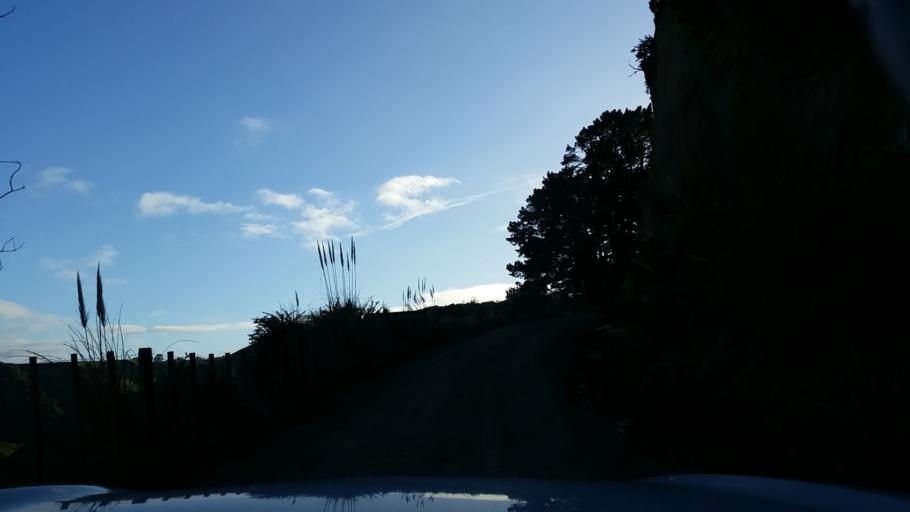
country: NZ
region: Taranaki
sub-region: South Taranaki District
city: Patea
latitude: -39.7580
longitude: 174.7387
